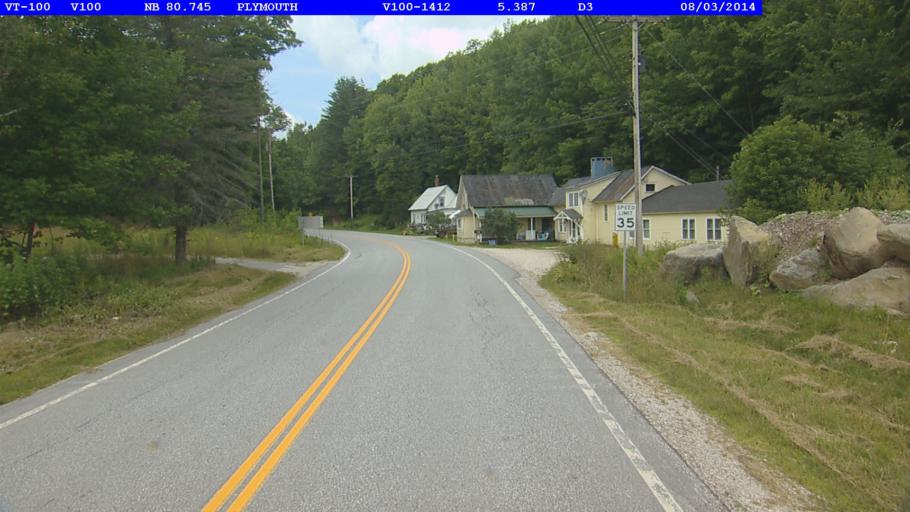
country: US
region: Vermont
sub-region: Windsor County
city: Woodstock
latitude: 43.5309
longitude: -72.7392
